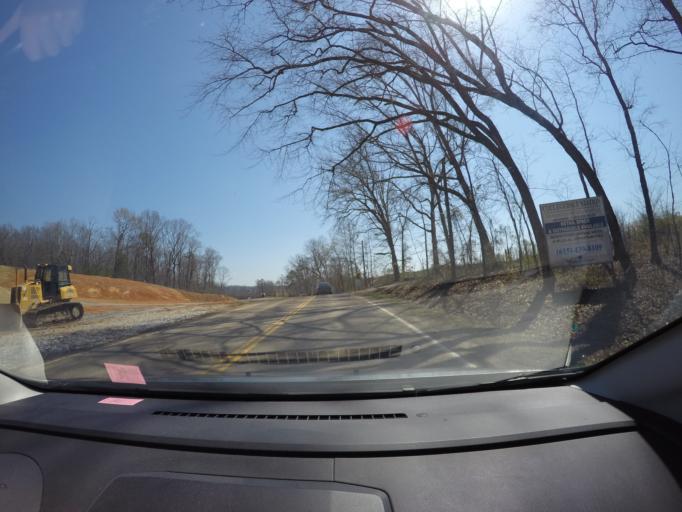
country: US
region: Tennessee
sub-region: Hamilton County
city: Collegedale
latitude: 35.0683
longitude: -85.0967
